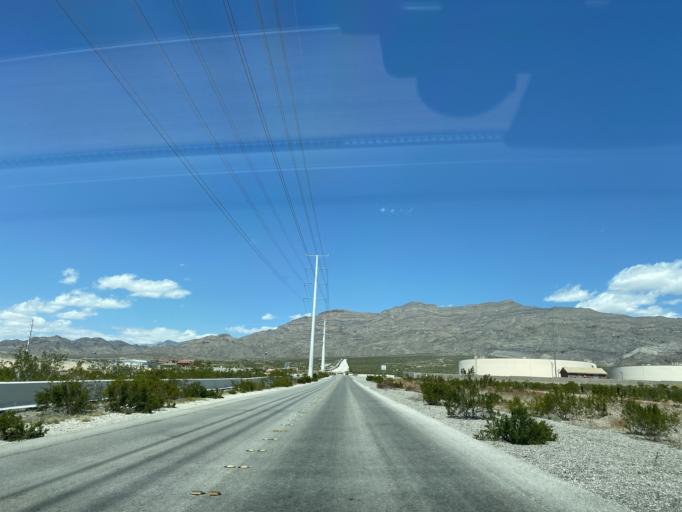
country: US
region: Nevada
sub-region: Clark County
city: North Las Vegas
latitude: 36.3319
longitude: -115.2071
